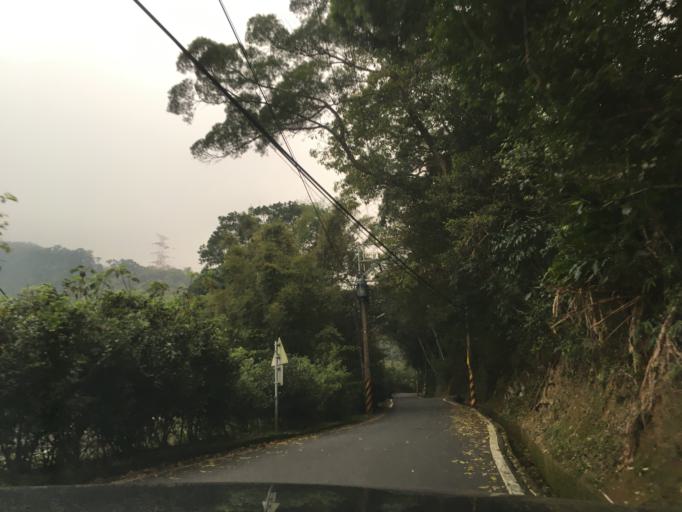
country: TW
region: Taiwan
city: Daxi
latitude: 24.8955
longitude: 121.3771
